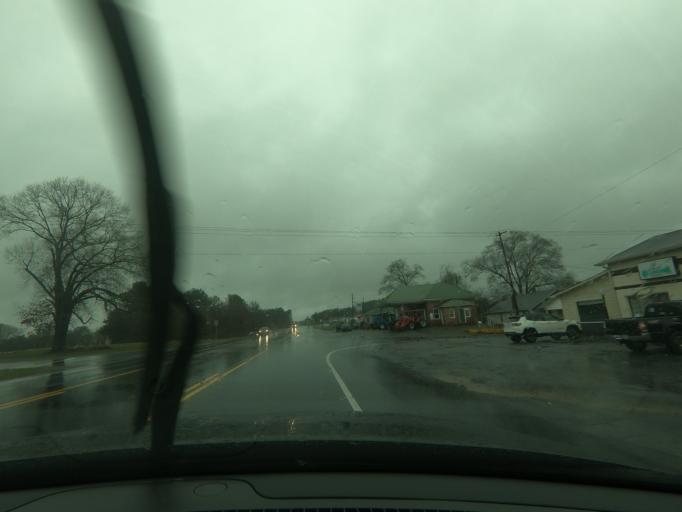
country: US
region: Georgia
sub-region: Bartow County
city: Adairsville
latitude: 34.3671
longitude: -84.9267
